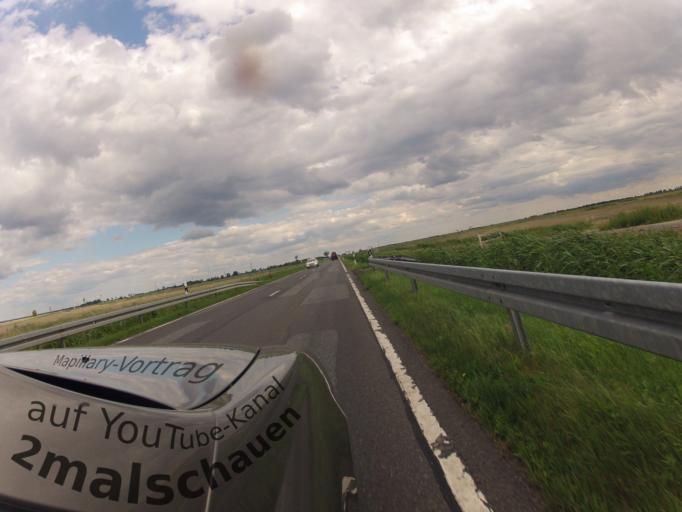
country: DE
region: Mecklenburg-Vorpommern
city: Lassan
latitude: 53.8722
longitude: 13.8101
